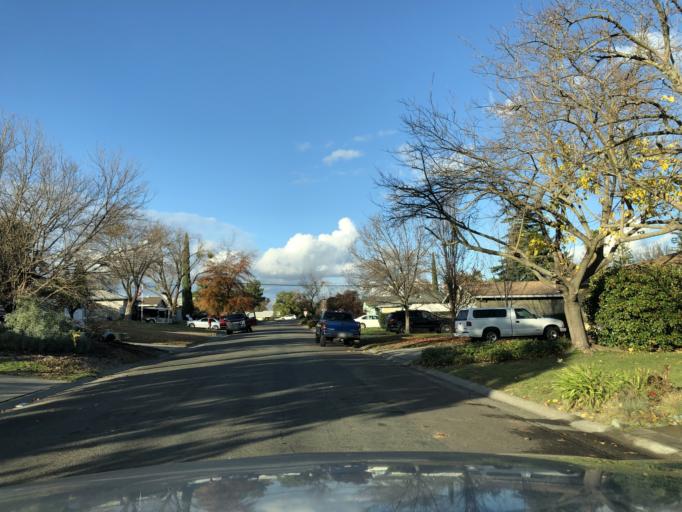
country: US
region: California
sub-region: Sacramento County
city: Foothill Farms
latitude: 38.6622
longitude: -121.3116
